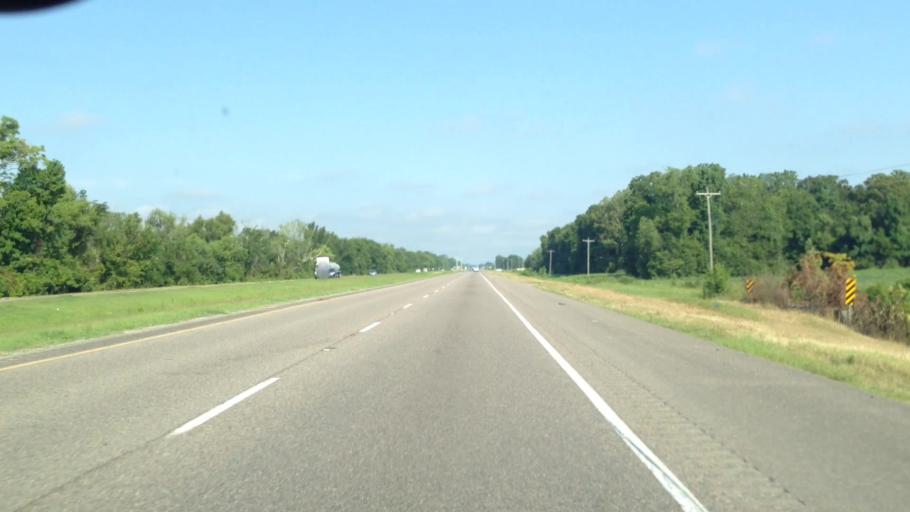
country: US
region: Louisiana
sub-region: West Baton Rouge Parish
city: Erwinville
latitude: 30.5163
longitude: -91.3572
